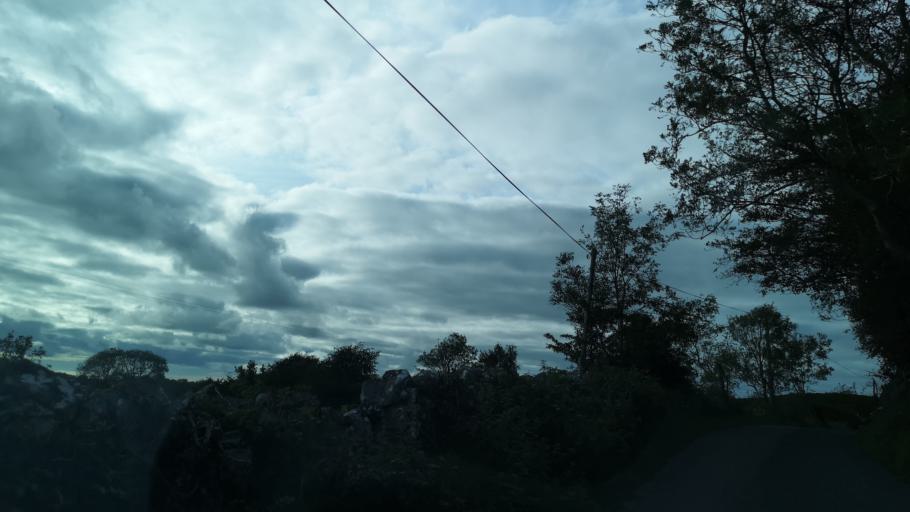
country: IE
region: Connaught
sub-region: County Galway
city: Ballinasloe
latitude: 53.3140
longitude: -8.1050
